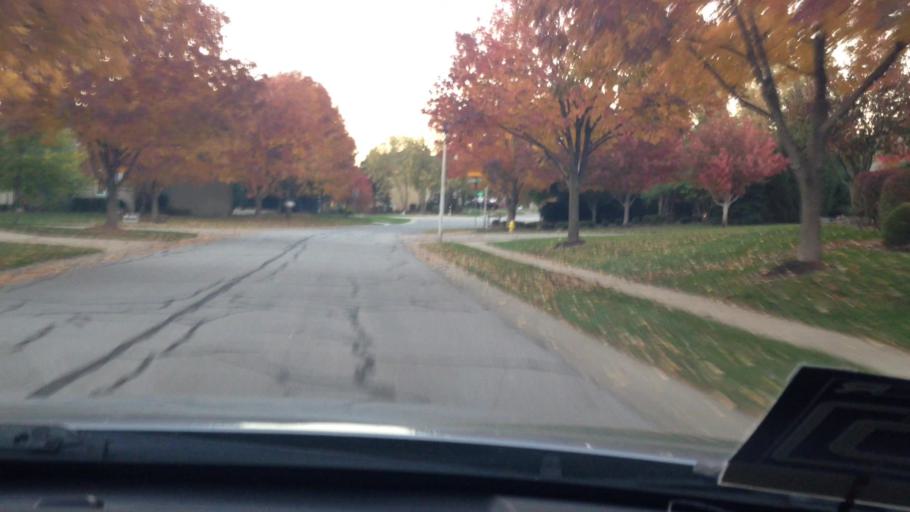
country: US
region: Kansas
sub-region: Johnson County
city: Lenexa
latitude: 38.8681
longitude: -94.7205
